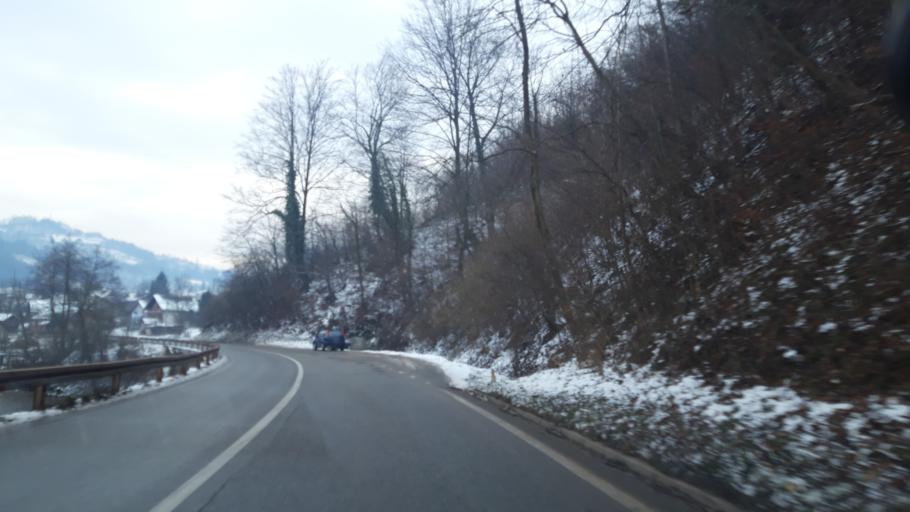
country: BA
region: Republika Srpska
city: Milici
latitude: 44.1890
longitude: 19.0709
